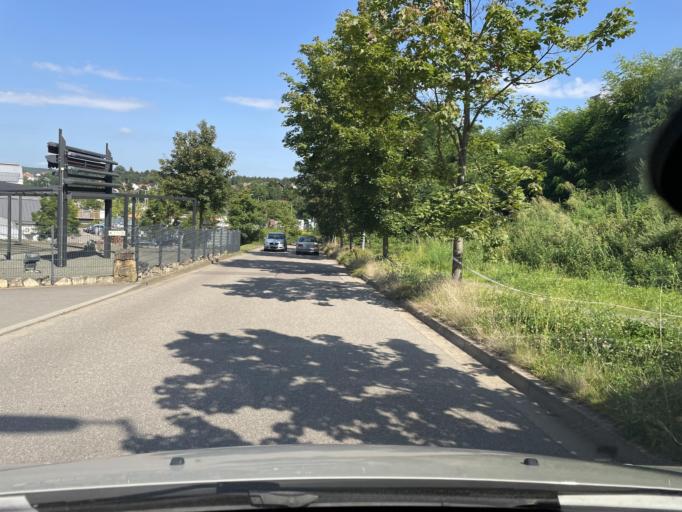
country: DE
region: Saarland
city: Sankt Ingbert
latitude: 49.2690
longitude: 7.1335
